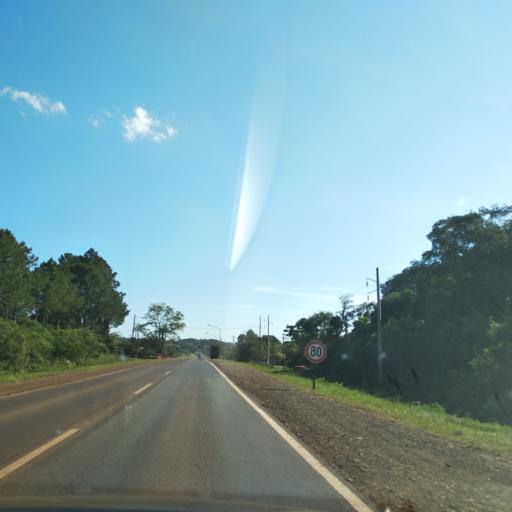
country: AR
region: Misiones
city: Jardin America
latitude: -27.0277
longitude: -55.2129
